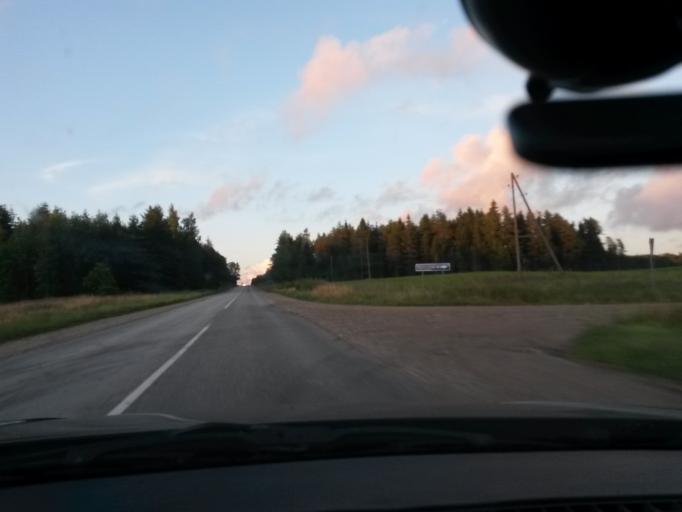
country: LV
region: Madonas Rajons
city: Madona
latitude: 56.8130
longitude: 26.1144
